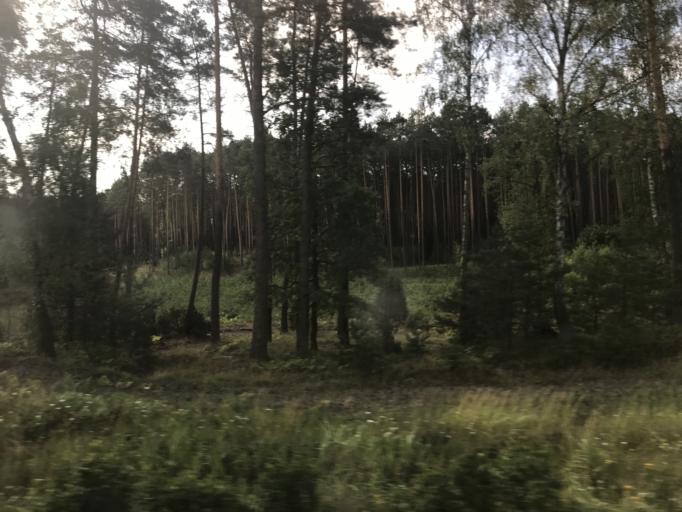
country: PL
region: Kujawsko-Pomorskie
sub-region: Powiat swiecki
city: Jezewo
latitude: 53.5585
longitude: 18.5589
